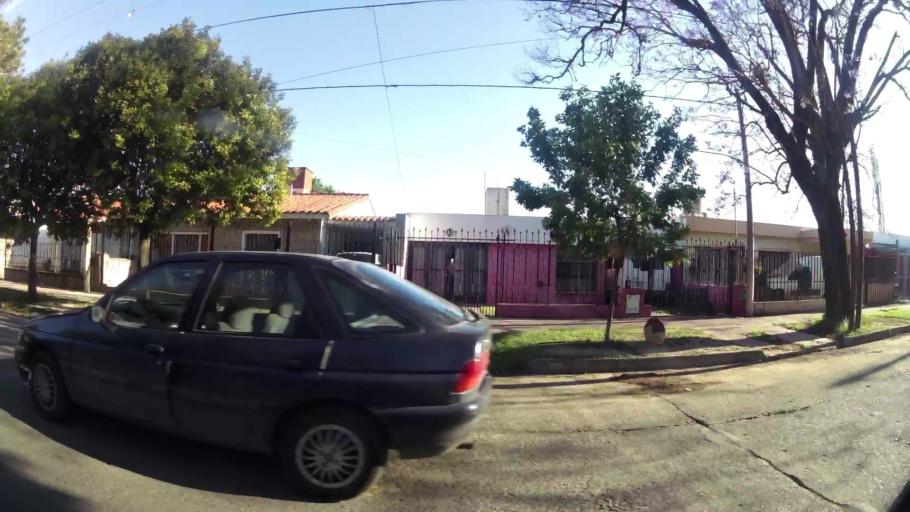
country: AR
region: Cordoba
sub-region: Departamento de Capital
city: Cordoba
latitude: -31.3767
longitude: -64.1788
